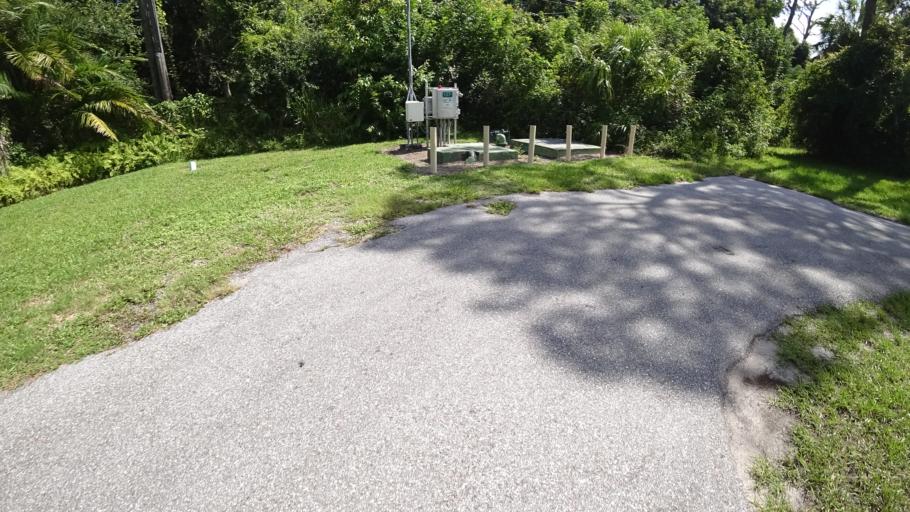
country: US
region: Florida
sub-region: Manatee County
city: Whitfield
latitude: 27.3899
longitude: -82.5655
